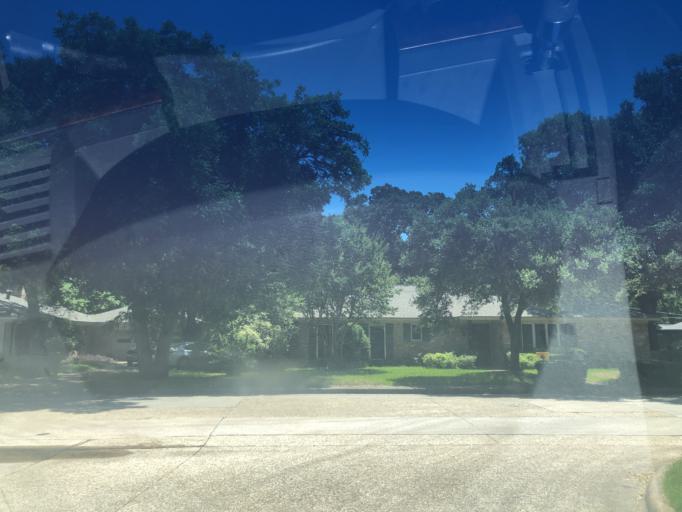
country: US
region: Texas
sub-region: Dallas County
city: Grand Prairie
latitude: 32.7759
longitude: -97.0360
